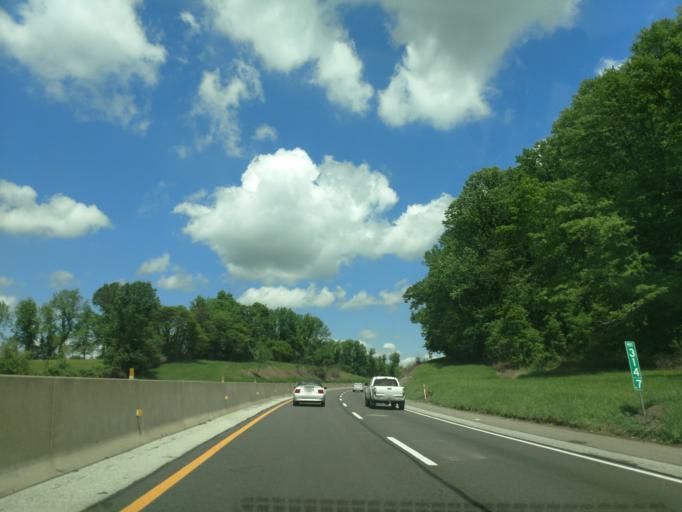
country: US
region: Pennsylvania
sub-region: Chester County
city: Chester Springs
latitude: 40.0639
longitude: -75.6196
